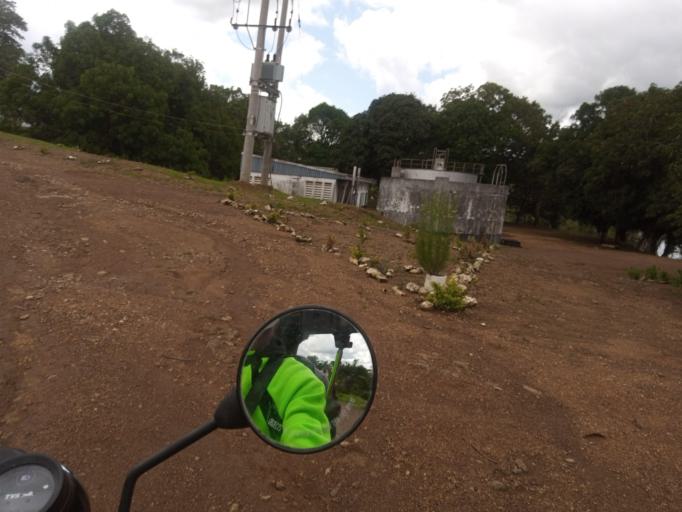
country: SL
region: Northern Province
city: Port Loko
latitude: 8.7616
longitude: -12.7751
